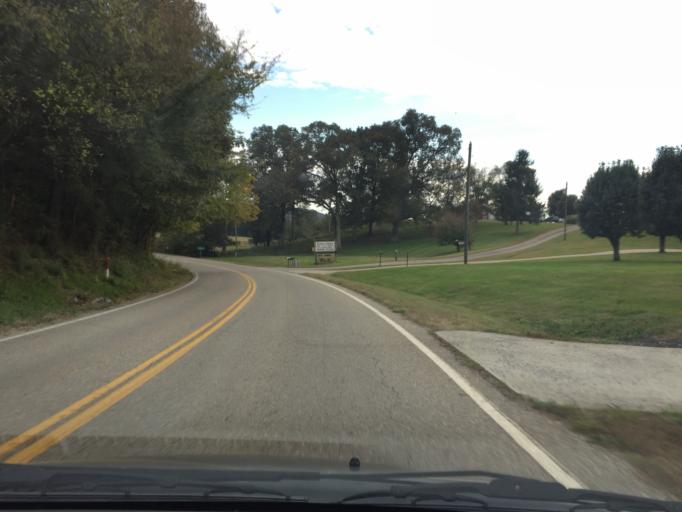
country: US
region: Tennessee
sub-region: Monroe County
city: Sweetwater
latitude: 35.6306
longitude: -84.5047
